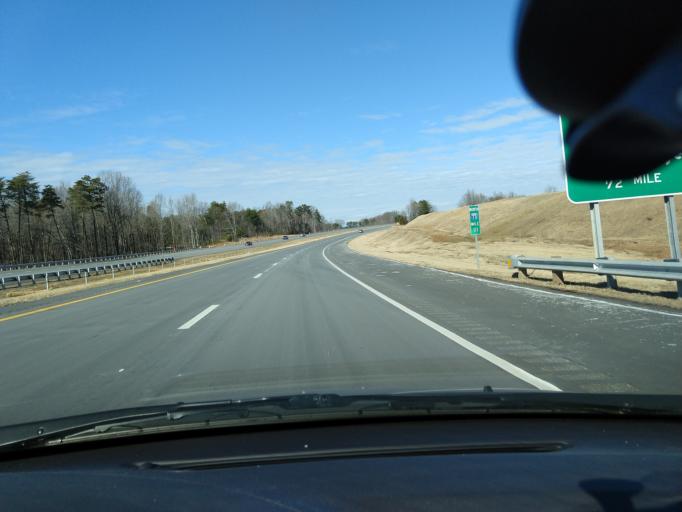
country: US
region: North Carolina
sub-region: Guilford County
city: Oak Ridge
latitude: 36.1276
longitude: -79.9650
